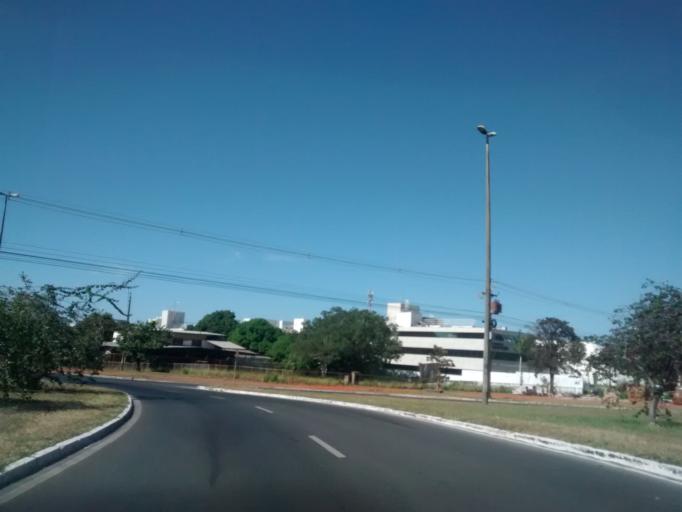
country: BR
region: Federal District
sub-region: Brasilia
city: Brasilia
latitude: -15.8276
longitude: -47.9037
